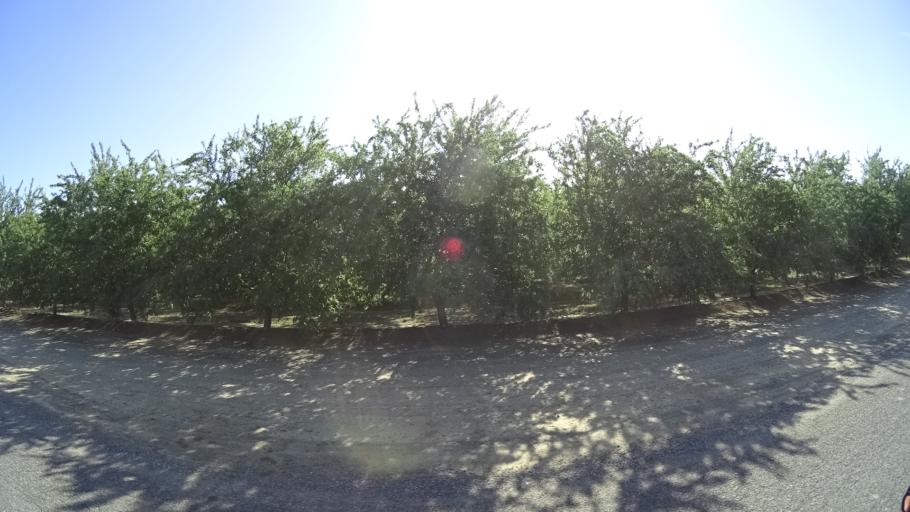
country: US
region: California
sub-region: Glenn County
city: Hamilton City
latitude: 39.6931
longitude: -122.0641
